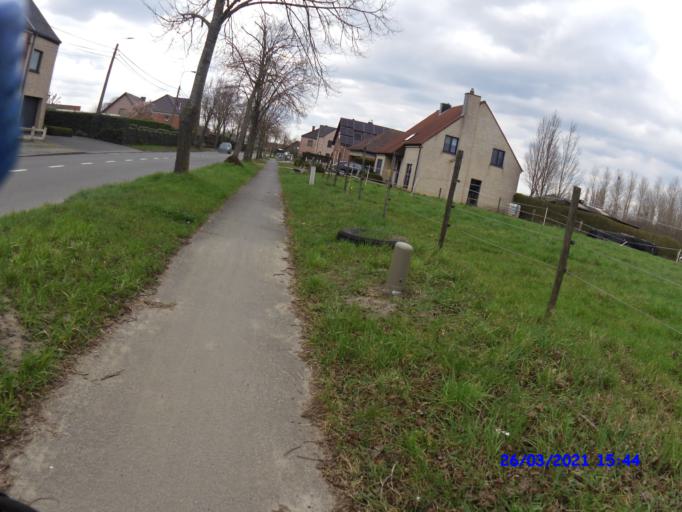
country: BE
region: Flanders
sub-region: Provincie Oost-Vlaanderen
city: Buggenhout
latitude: 51.0114
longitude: 4.1795
